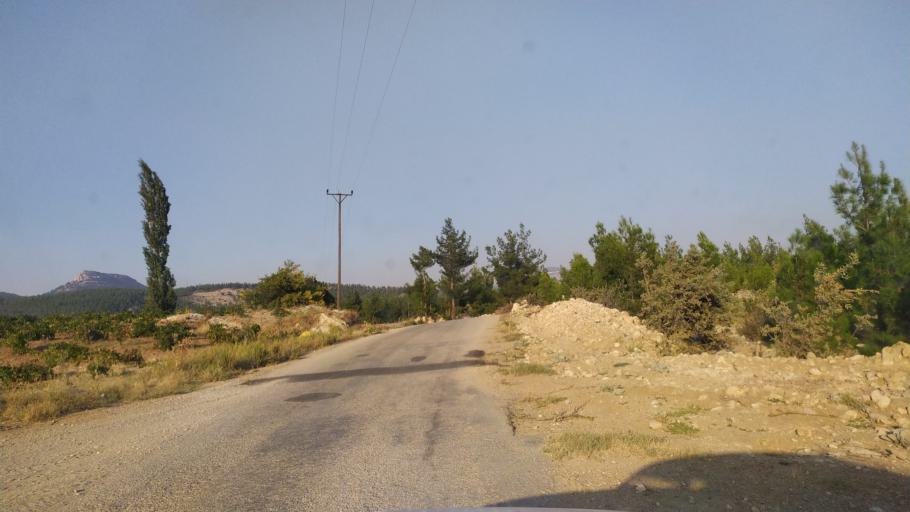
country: TR
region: Mersin
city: Mut
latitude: 36.6864
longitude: 33.1952
